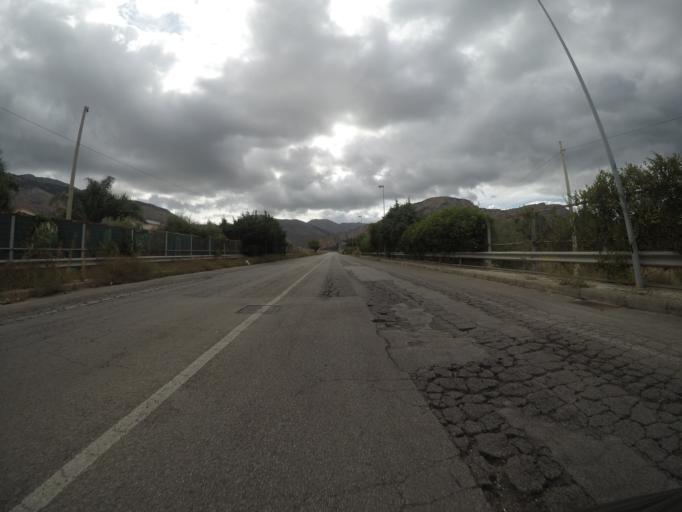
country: IT
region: Sicily
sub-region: Palermo
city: Capaci
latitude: 38.1706
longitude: 13.2204
